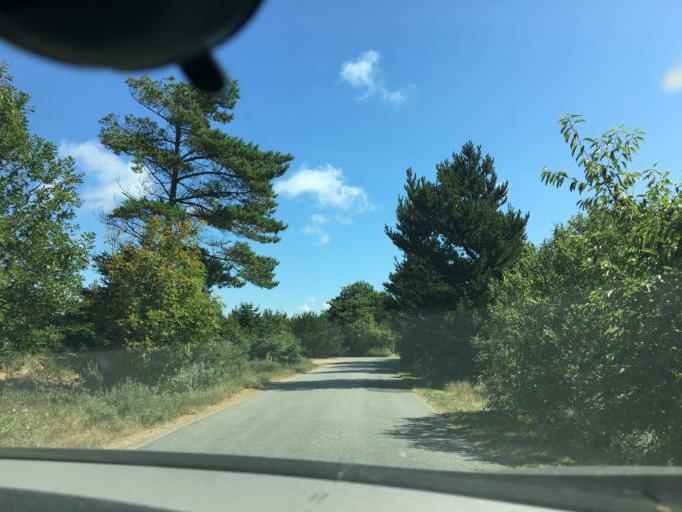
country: DK
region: South Denmark
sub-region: Varde Kommune
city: Oksbol
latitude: 55.7365
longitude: 8.2106
